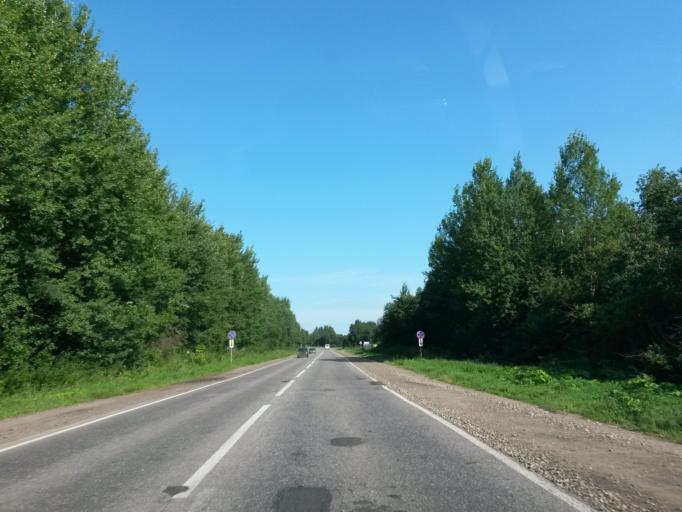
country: RU
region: Jaroslavl
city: Yaroslavl
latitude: 57.5332
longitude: 39.8736
